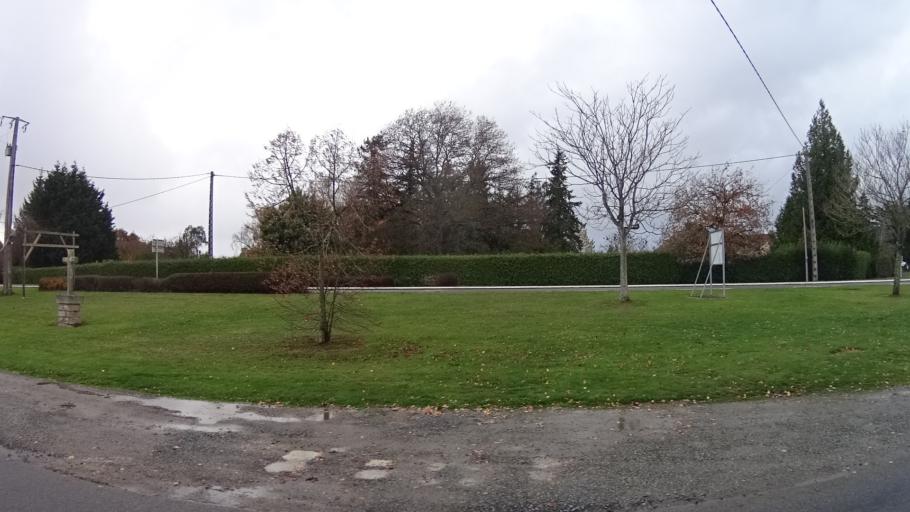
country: FR
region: Brittany
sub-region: Departement du Morbihan
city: Rieux
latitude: 47.5749
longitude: -2.1287
